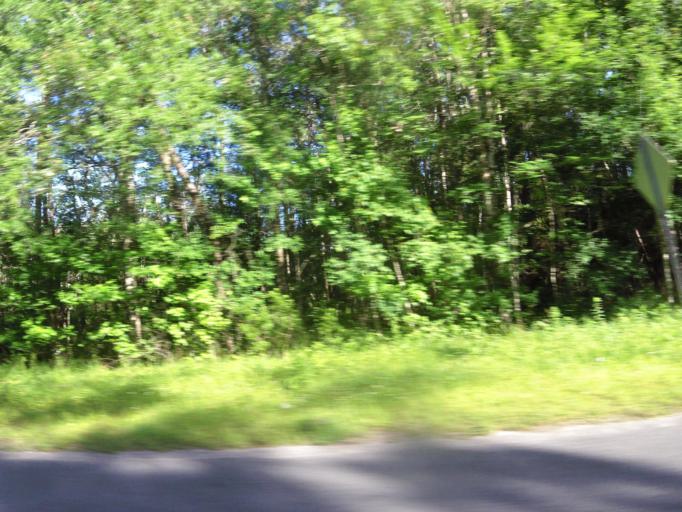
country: US
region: Florida
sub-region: Nassau County
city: Nassau Village-Ratliff
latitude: 30.5106
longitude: -81.7963
